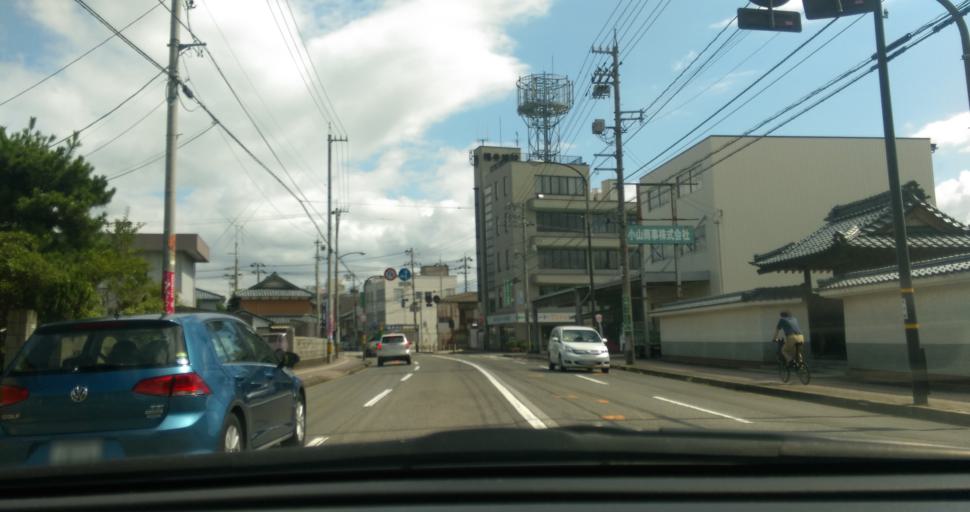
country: JP
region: Fukui
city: Fukui-shi
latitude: 36.0786
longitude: 136.2094
